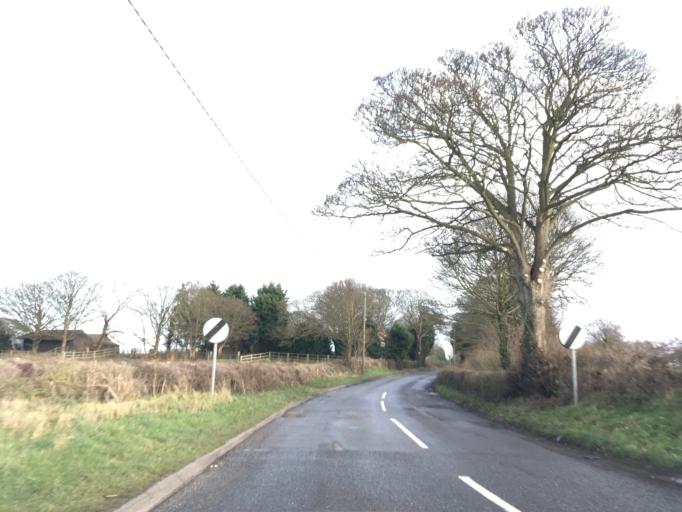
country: GB
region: England
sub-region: Nottinghamshire
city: South Collingham
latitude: 53.1775
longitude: -0.7642
